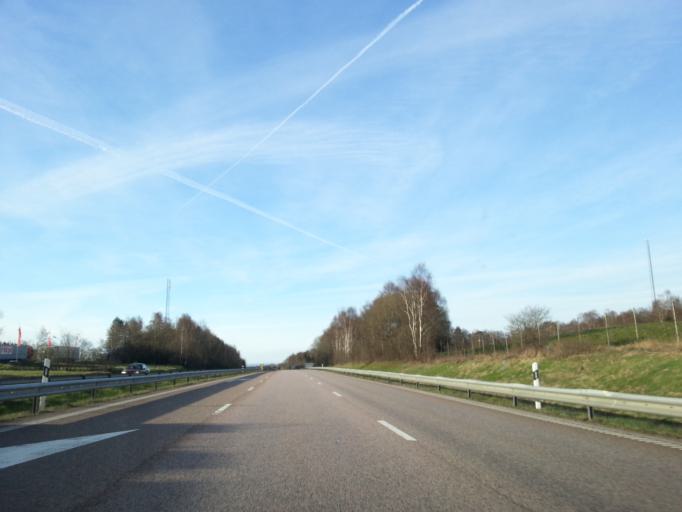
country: SE
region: Skane
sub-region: Bastads Kommun
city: Bastad
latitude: 56.3880
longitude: 12.9384
